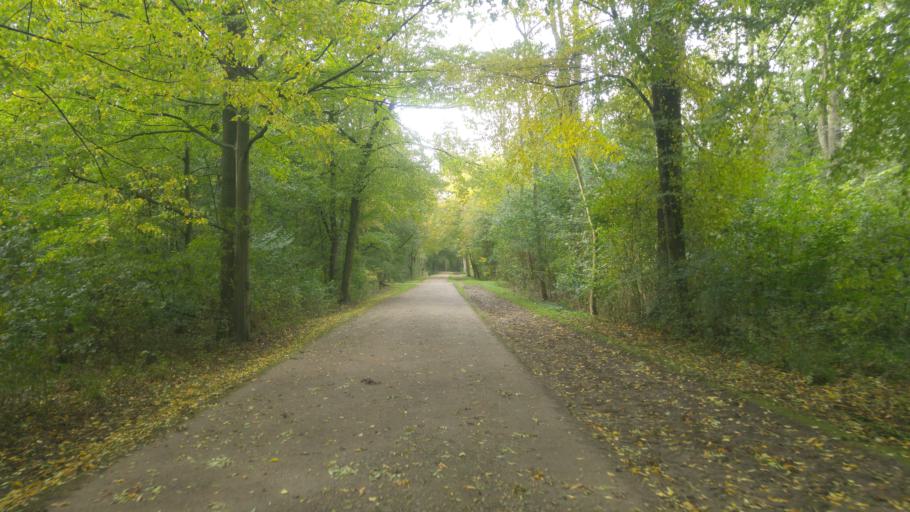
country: DE
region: Bremen
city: Bremen
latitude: 53.1084
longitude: 8.8299
